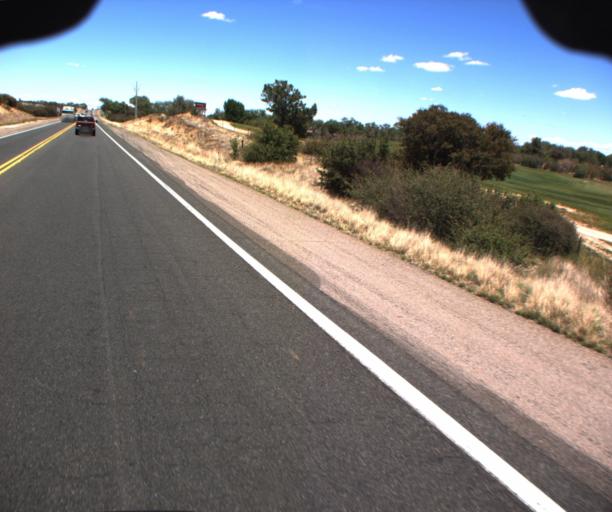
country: US
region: Arizona
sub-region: Yavapai County
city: Prescott
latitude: 34.6362
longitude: -112.4302
